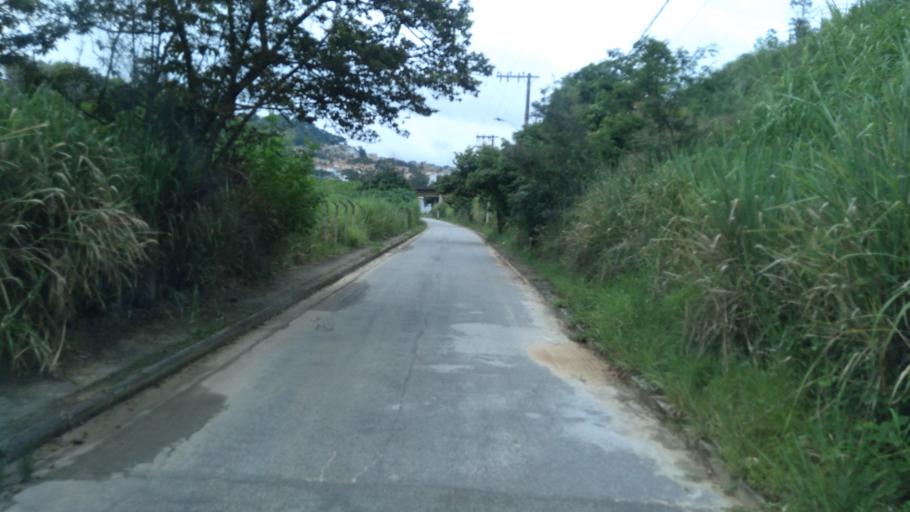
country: BR
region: Minas Gerais
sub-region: Santa Luzia
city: Santa Luzia
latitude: -19.8395
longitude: -43.8711
